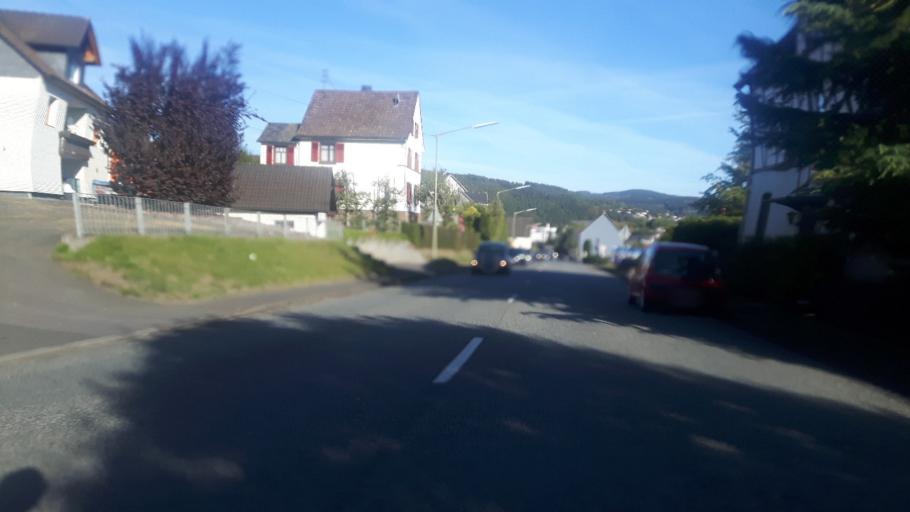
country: DE
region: Rheinland-Pfalz
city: Wallmenroth
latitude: 50.7967
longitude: 7.8387
